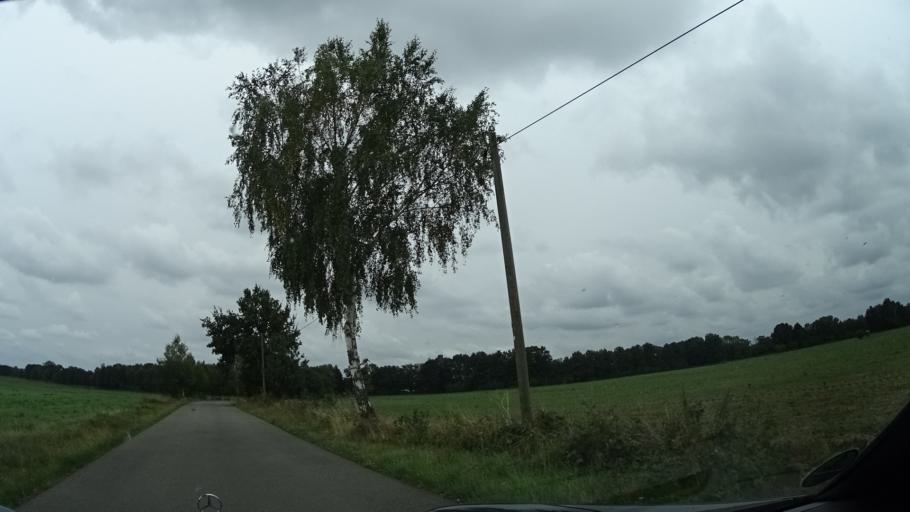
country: DE
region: Brandenburg
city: Neuruppin
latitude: 52.9642
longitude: 12.7614
